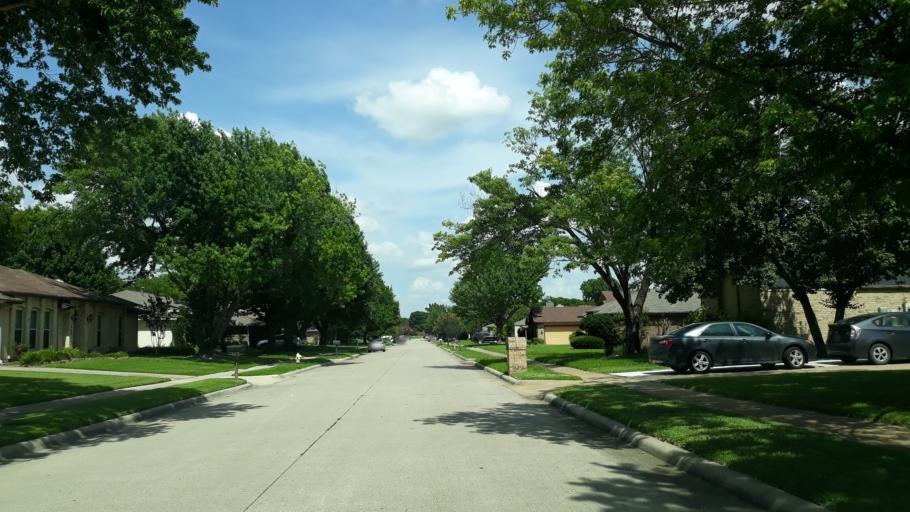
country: US
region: Texas
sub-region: Dallas County
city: Coppell
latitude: 32.9580
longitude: -97.0043
